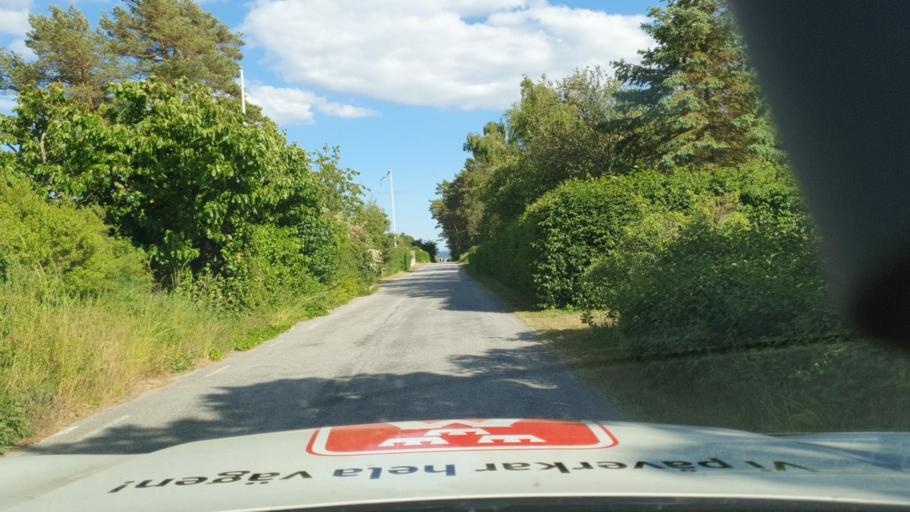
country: SE
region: Skane
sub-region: Simrishamns Kommun
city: Simrishamn
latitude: 55.4357
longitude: 14.2319
